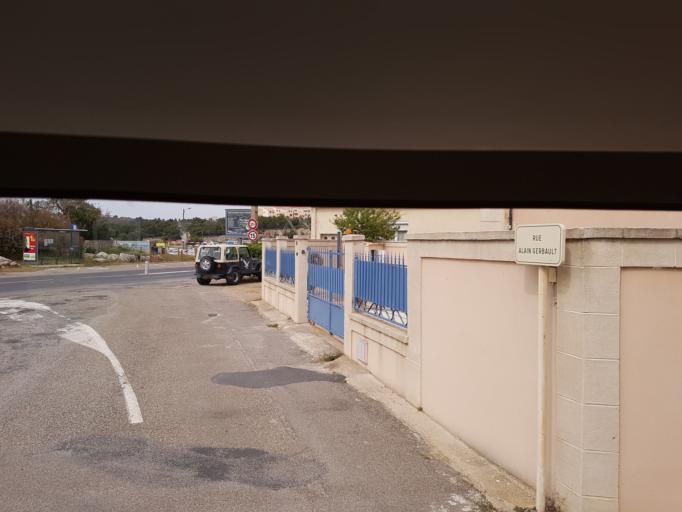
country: FR
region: Languedoc-Roussillon
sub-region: Departement de l'Aude
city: Fleury
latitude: 43.1697
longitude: 3.1795
